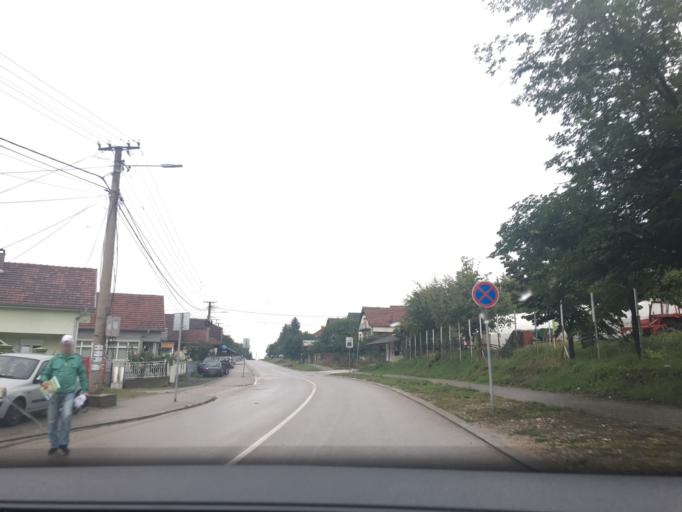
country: RS
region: Central Serbia
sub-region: Nisavski Okrug
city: Aleksinac
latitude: 43.5428
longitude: 21.7007
